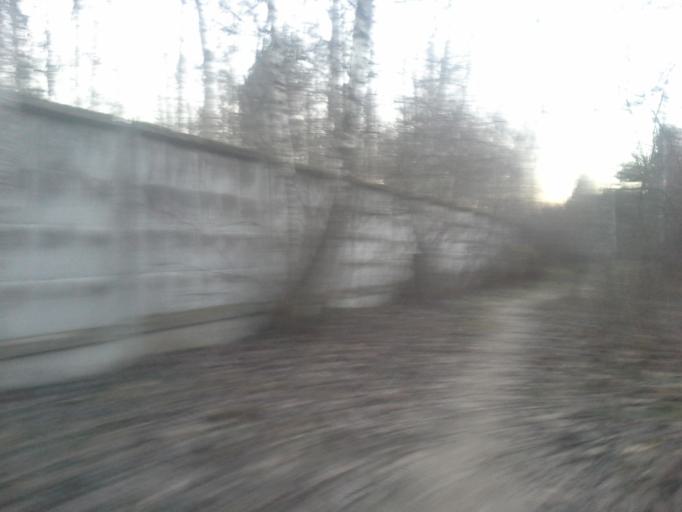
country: RU
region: Moscow
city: Tolstopal'tsevo
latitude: 55.6153
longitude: 37.2165
